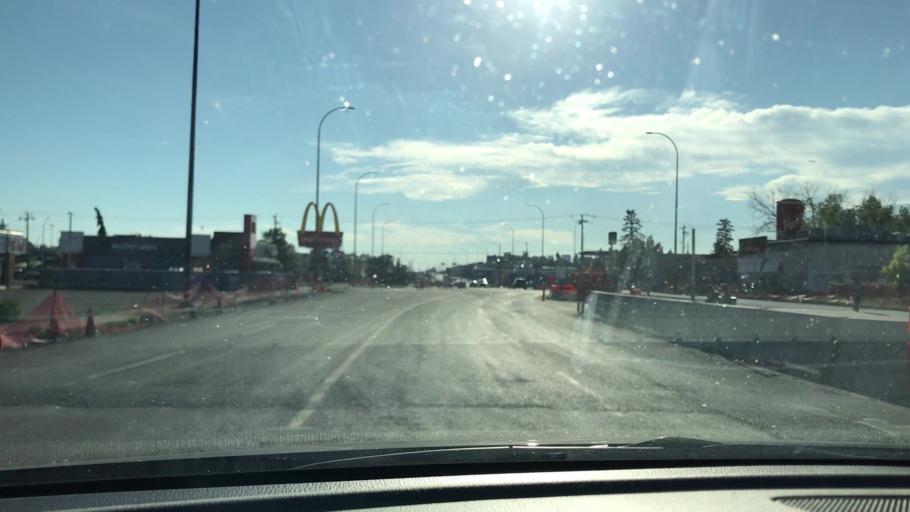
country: CA
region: Alberta
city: Calgary
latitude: 51.0378
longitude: -113.9658
